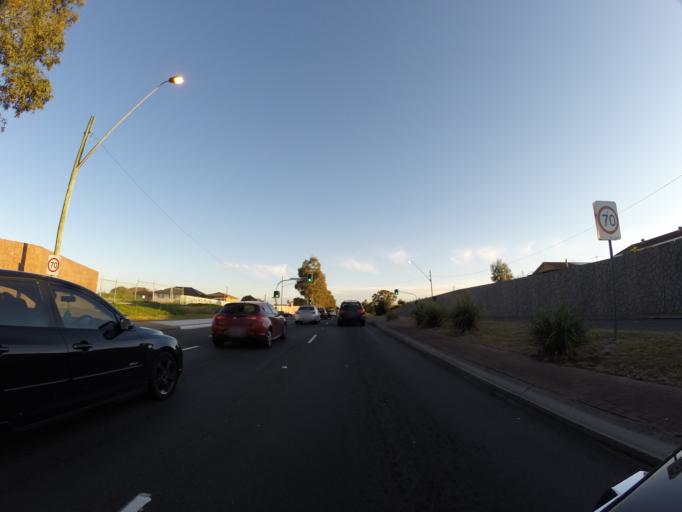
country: AU
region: New South Wales
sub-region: Fairfield
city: Cecil Park
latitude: -33.8770
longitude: 150.8682
